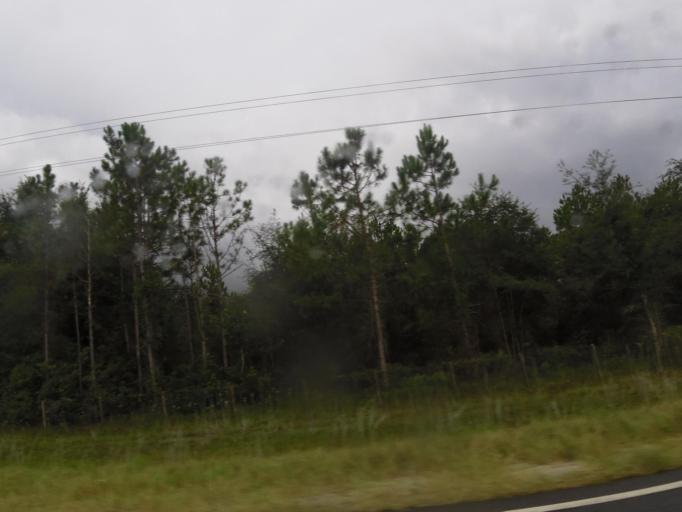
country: US
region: Florida
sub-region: Baker County
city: Macclenny
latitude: 30.3688
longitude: -82.1458
